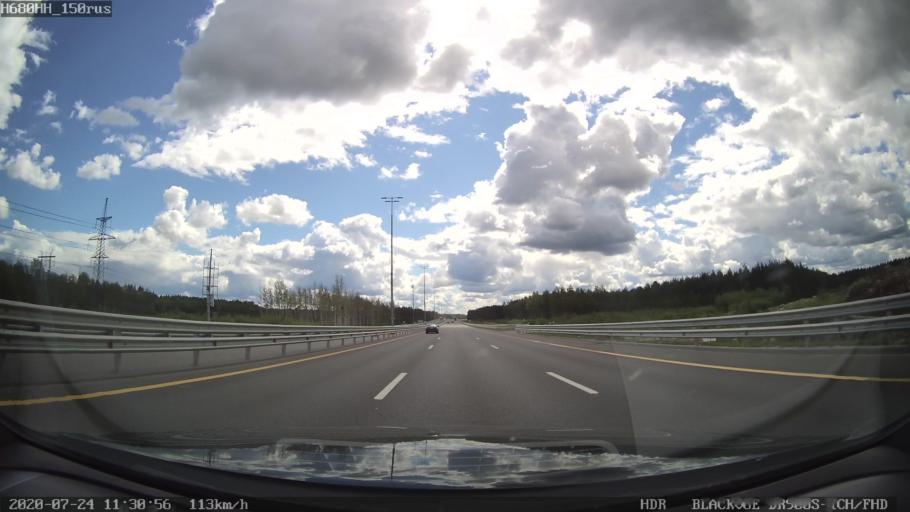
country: RU
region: Leningrad
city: Krasnyy Bor
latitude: 59.6639
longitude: 30.6230
